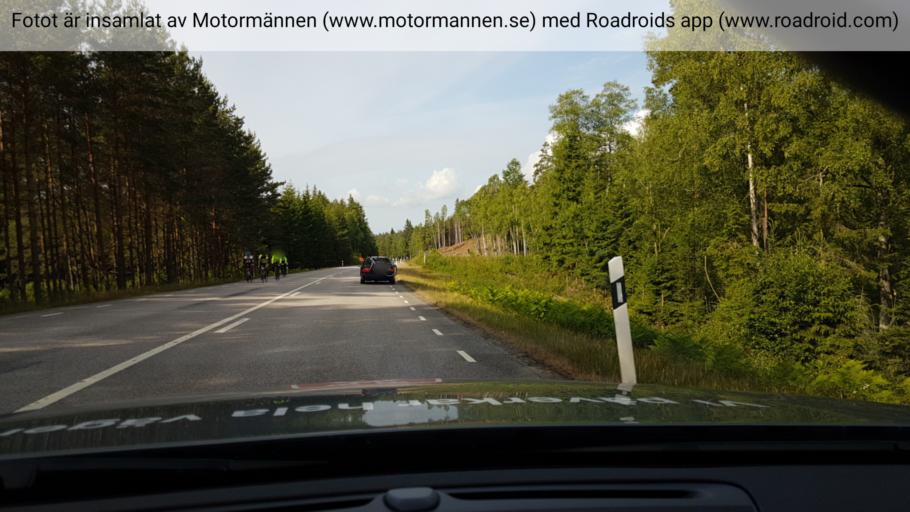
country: SE
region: Vaestra Goetaland
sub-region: Karlsborgs Kommun
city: Karlsborg
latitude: 58.6541
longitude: 14.5824
